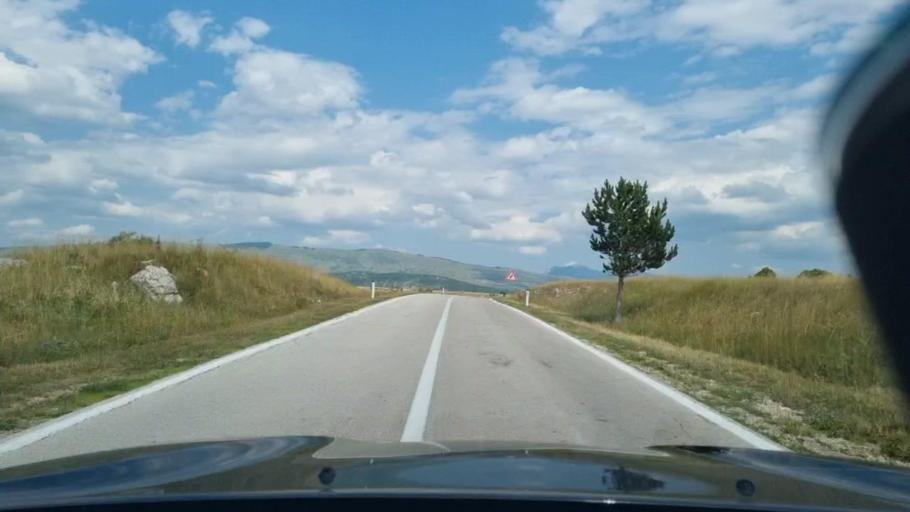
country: BA
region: Federation of Bosnia and Herzegovina
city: Bosansko Grahovo
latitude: 44.1584
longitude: 16.4007
